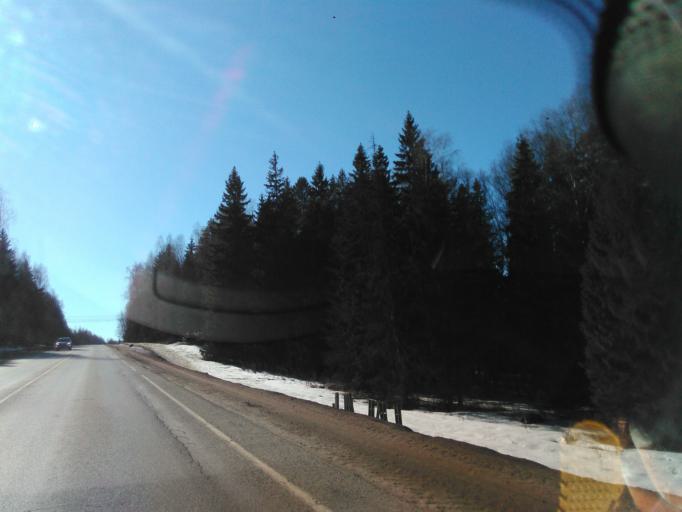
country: RU
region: Moskovskaya
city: Yermolino
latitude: 56.1273
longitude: 37.3472
